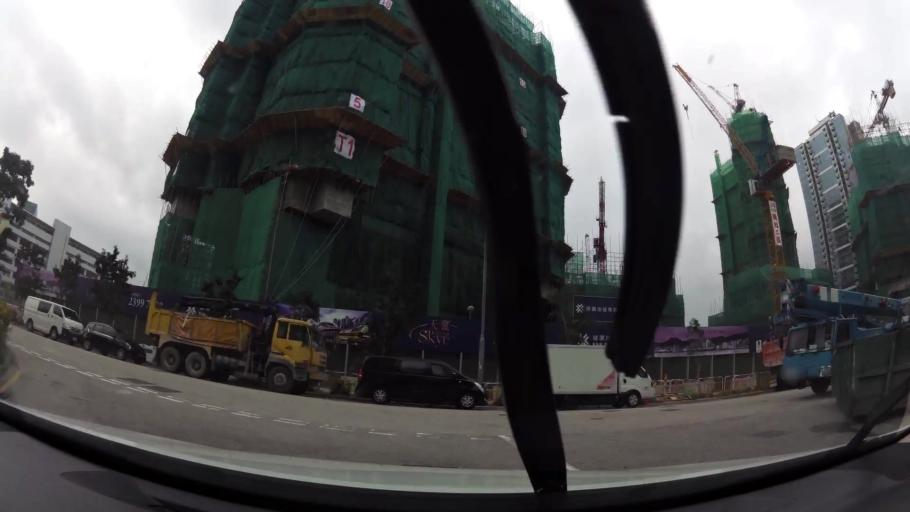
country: HK
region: Kowloon City
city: Kowloon
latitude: 22.3284
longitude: 114.2028
